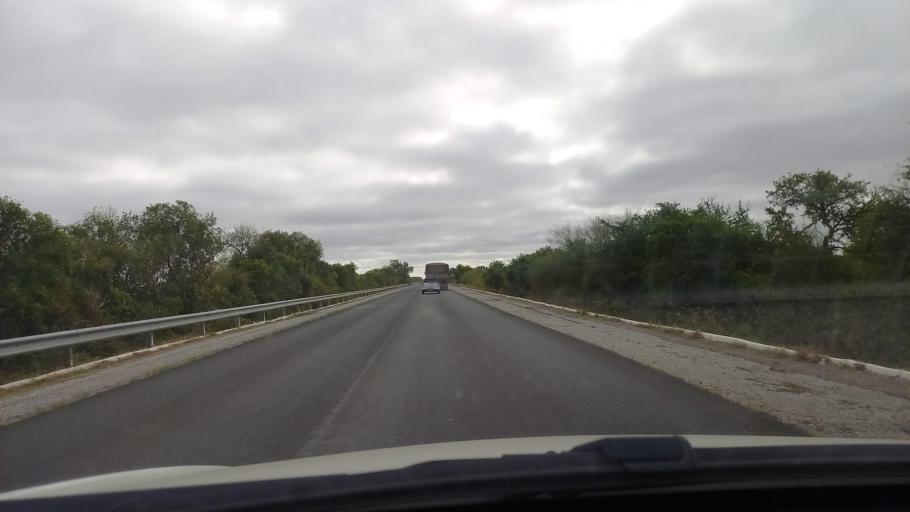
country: BR
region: Rio Grande do Sul
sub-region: Dom Pedrito
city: Dom Pedrito
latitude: -30.9507
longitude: -54.7054
